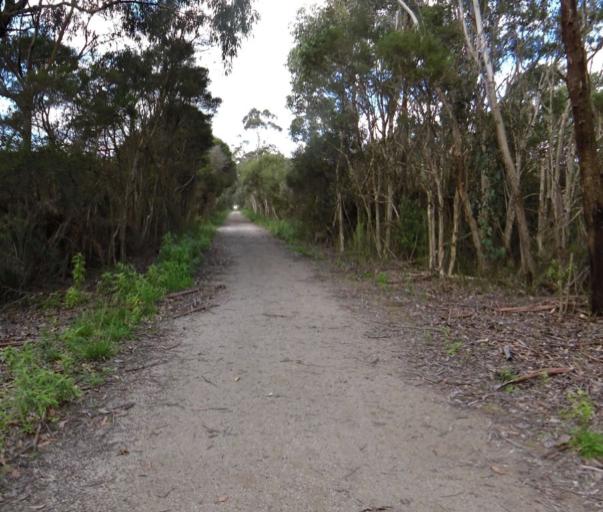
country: AU
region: Victoria
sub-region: Bass Coast
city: North Wonthaggi
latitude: -38.5821
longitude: 146.0339
